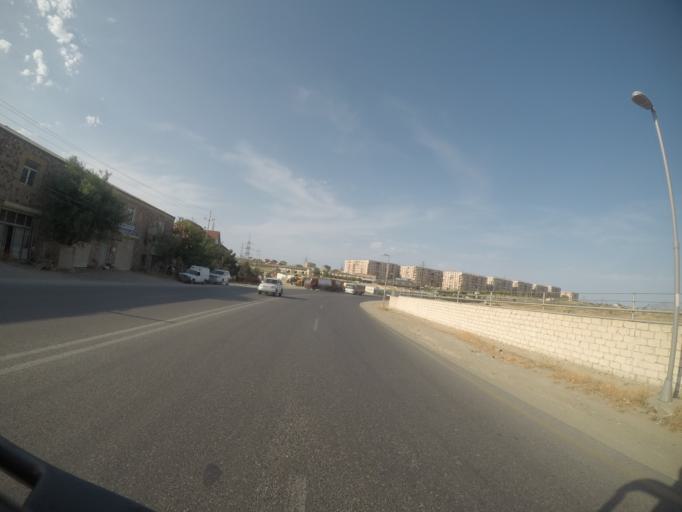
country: AZ
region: Baki
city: Binagadi
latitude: 40.4796
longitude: 49.8347
